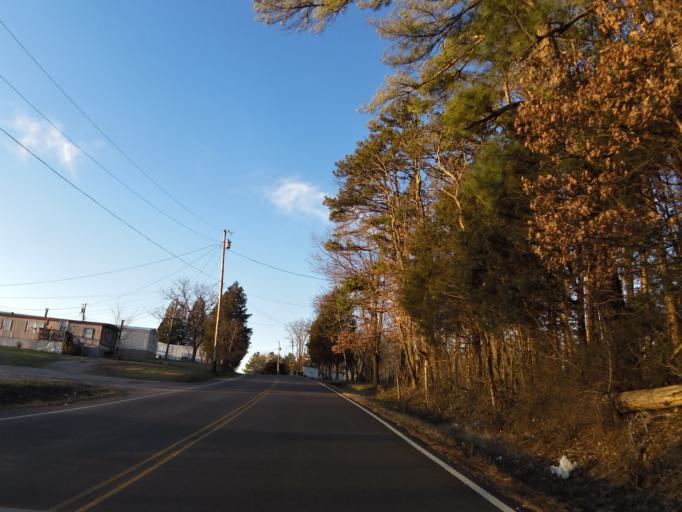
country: US
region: Tennessee
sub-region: Knox County
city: Mascot
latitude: 36.0272
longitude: -83.7296
